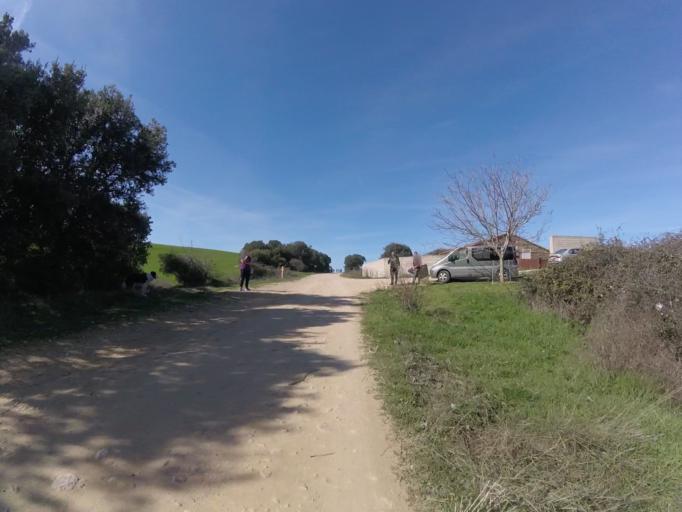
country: ES
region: Navarre
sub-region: Provincia de Navarra
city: Oteiza
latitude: 42.6422
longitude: -1.9541
